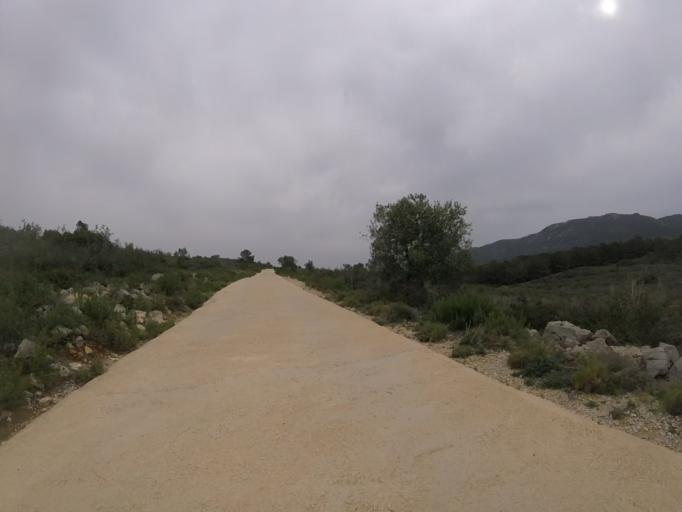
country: ES
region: Valencia
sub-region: Provincia de Castello
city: Alcala de Xivert
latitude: 40.2955
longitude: 0.2558
